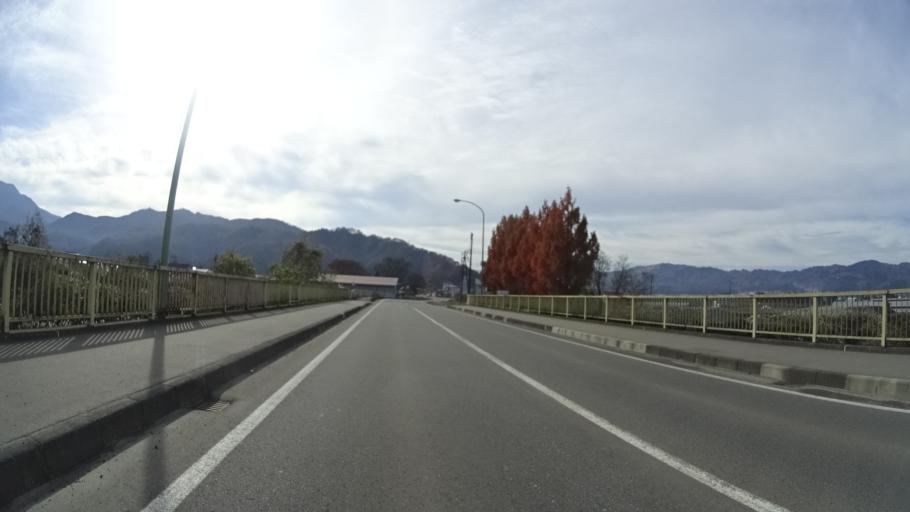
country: JP
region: Niigata
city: Muikamachi
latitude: 37.0862
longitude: 138.9096
